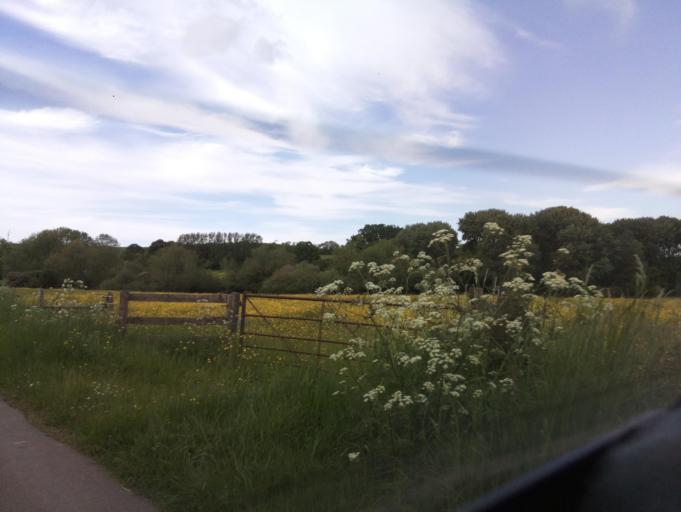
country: GB
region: England
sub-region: Gloucestershire
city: Moreton in Marsh
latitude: 52.0289
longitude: -1.7183
